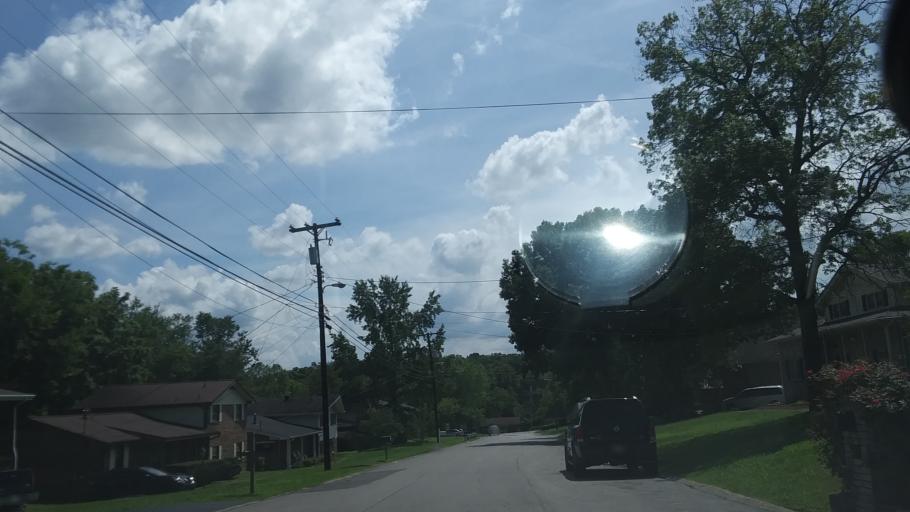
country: US
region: Tennessee
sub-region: Rutherford County
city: La Vergne
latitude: 36.0814
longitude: -86.6319
